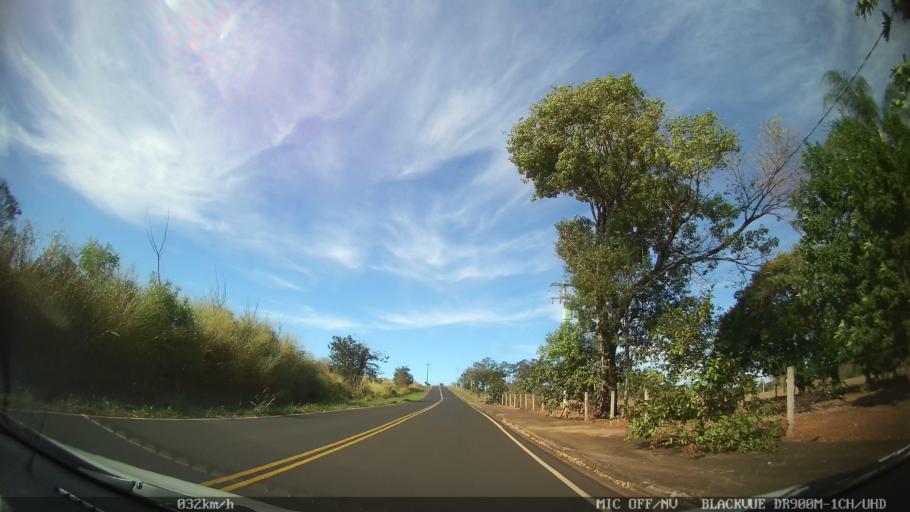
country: BR
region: Sao Paulo
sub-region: Sao Jose Do Rio Preto
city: Sao Jose do Rio Preto
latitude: -20.7958
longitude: -49.3162
